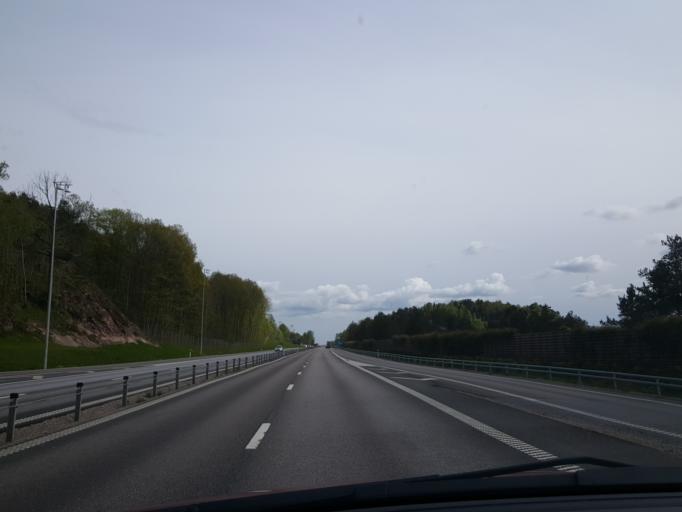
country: SE
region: Vaestra Goetaland
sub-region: Lilla Edets Kommun
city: Lilla Edet
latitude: 58.1429
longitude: 12.1354
